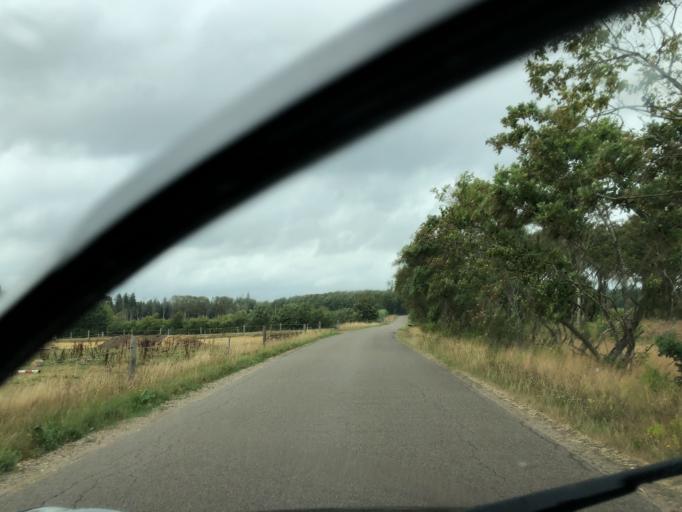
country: DK
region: Central Jutland
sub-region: Holstebro Kommune
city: Ulfborg
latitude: 56.1550
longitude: 8.4076
